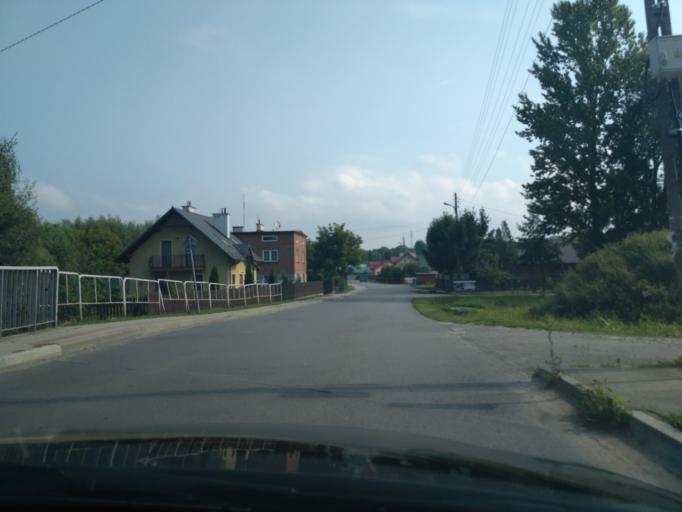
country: PL
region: Subcarpathian Voivodeship
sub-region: Powiat rzeszowski
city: Niechobrz
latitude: 49.9989
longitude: 21.8879
